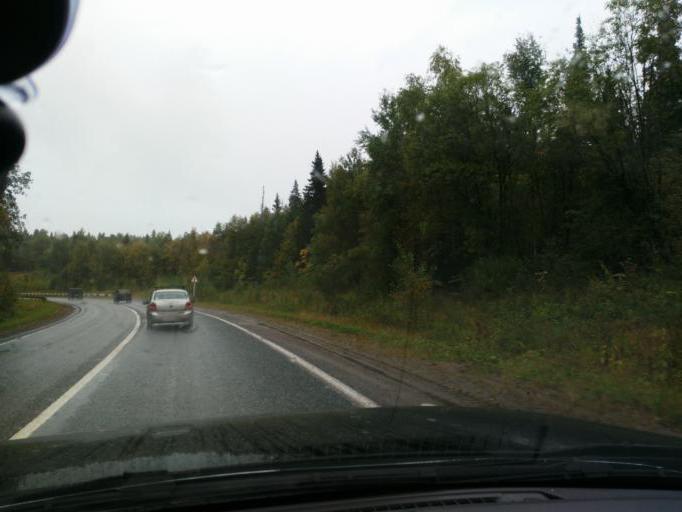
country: RU
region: Perm
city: Yugo-Kamskiy
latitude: 57.6030
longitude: 55.6560
